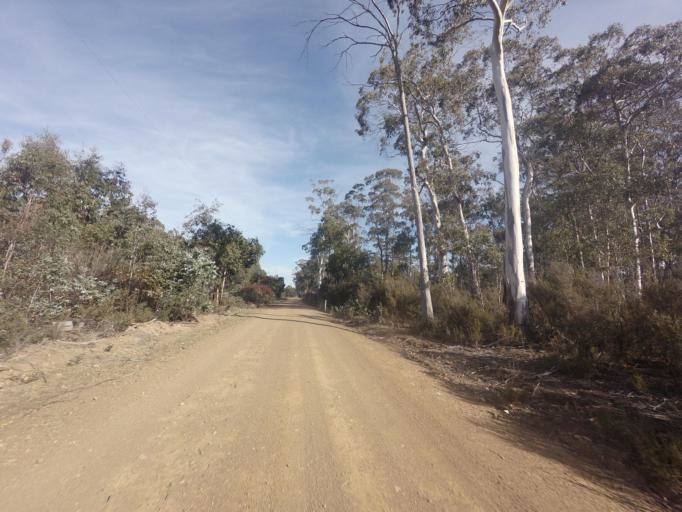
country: AU
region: Tasmania
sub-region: Sorell
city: Sorell
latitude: -42.5040
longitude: 147.4785
